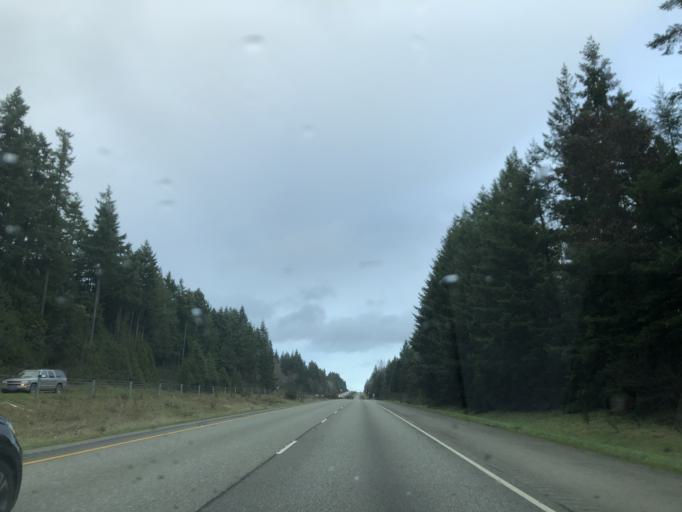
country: US
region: Washington
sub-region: Kitsap County
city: Bangor Trident Base
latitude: 47.7113
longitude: -122.6815
